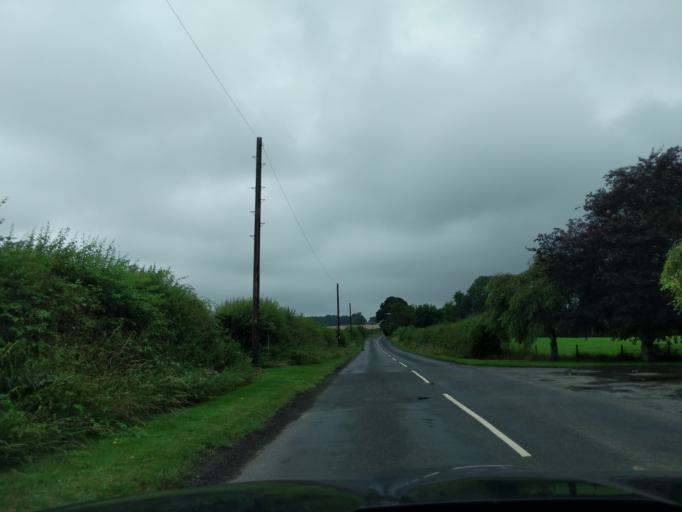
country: GB
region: England
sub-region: Northumberland
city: Ford
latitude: 55.6693
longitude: -2.1020
